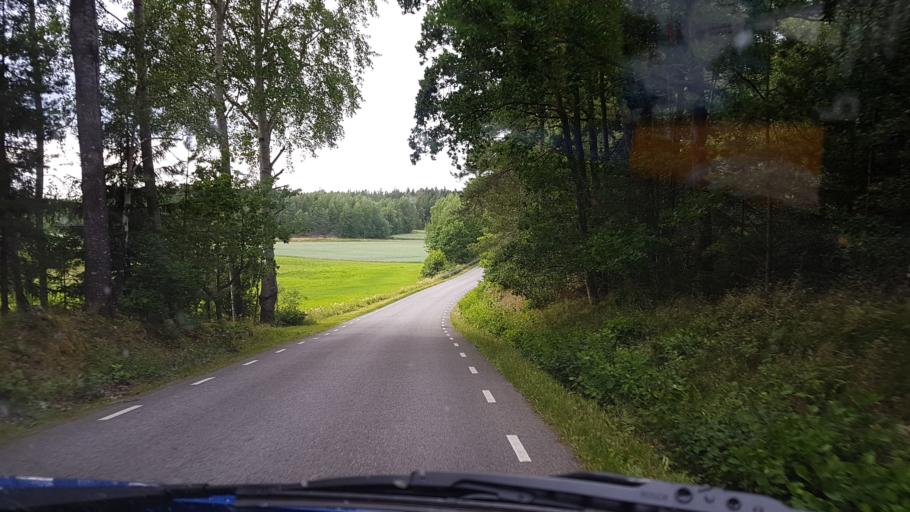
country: SE
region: OEstergoetland
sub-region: Valdemarsviks Kommun
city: Gusum
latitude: 58.4618
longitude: 16.5846
